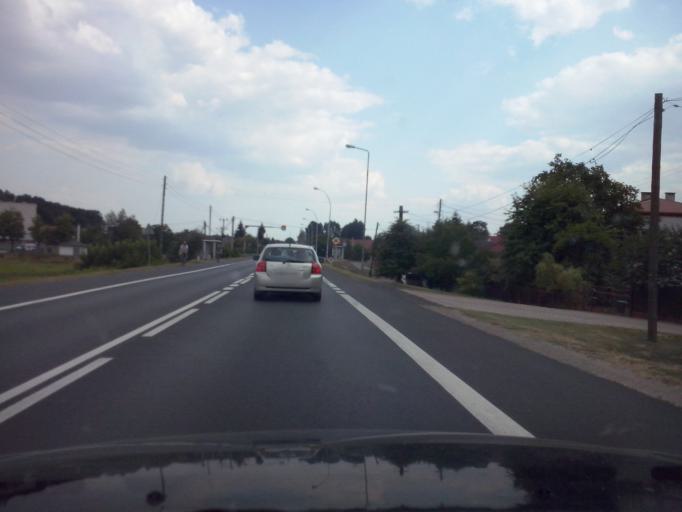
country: PL
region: Subcarpathian Voivodeship
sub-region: Powiat nizanski
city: Nisko
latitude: 50.5292
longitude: 22.1102
